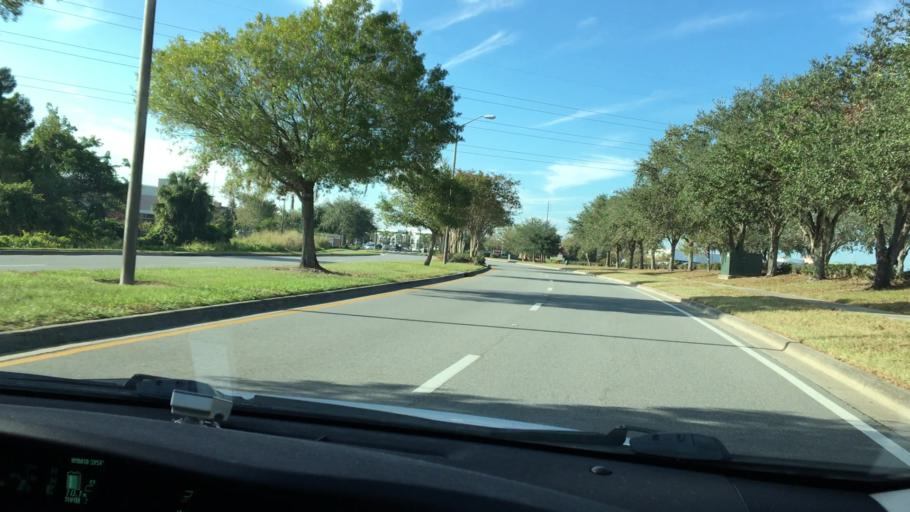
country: US
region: Florida
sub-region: Seminole County
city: Lake Mary
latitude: 28.8017
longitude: -81.3382
